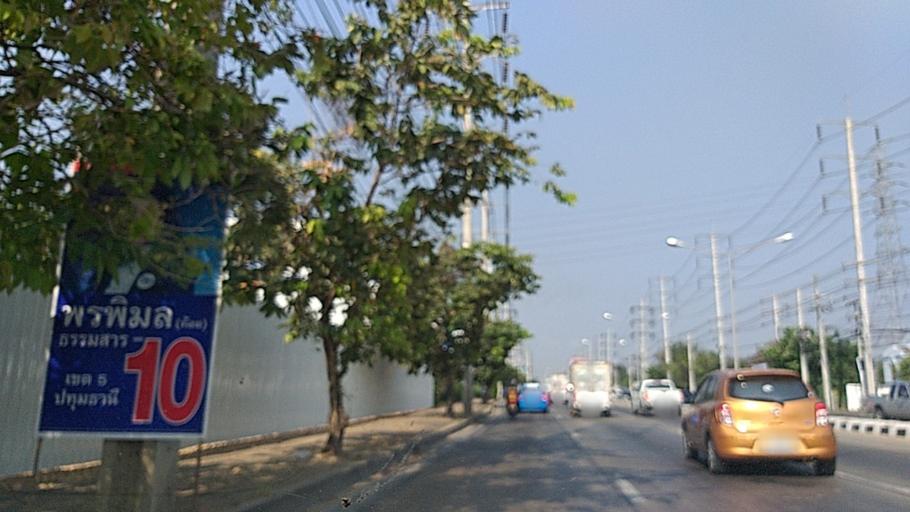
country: TH
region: Pathum Thani
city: Lam Luk Ka
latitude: 13.9334
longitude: 100.7019
